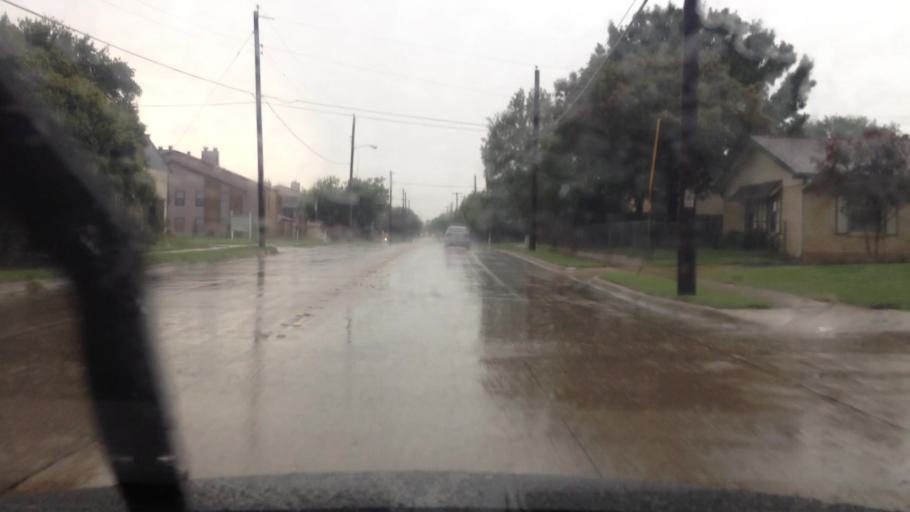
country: US
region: Texas
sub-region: Tarrant County
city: North Richland Hills
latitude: 32.8390
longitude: -97.2193
